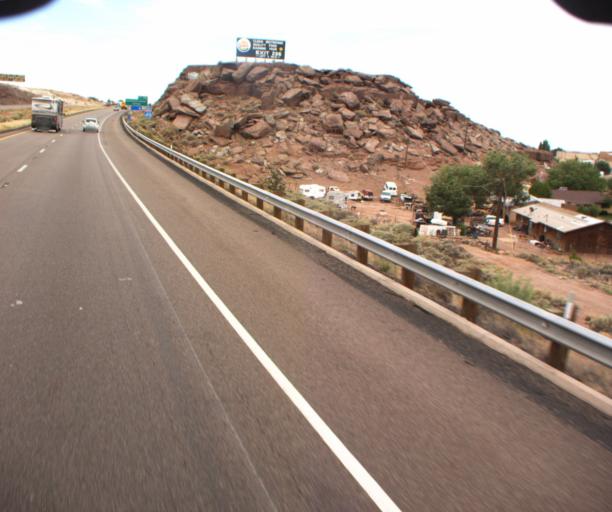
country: US
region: Arizona
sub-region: Navajo County
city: Holbrook
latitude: 34.9092
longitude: -110.1769
